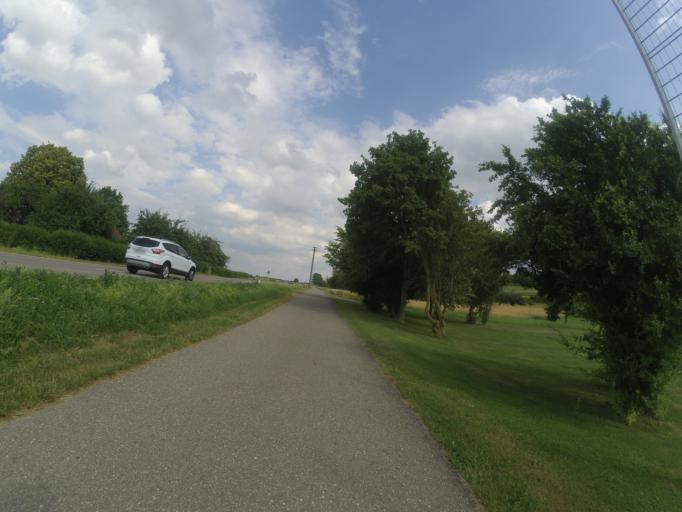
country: DE
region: Baden-Wuerttemberg
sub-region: Tuebingen Region
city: Griesingen
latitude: 48.2712
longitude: 9.7752
